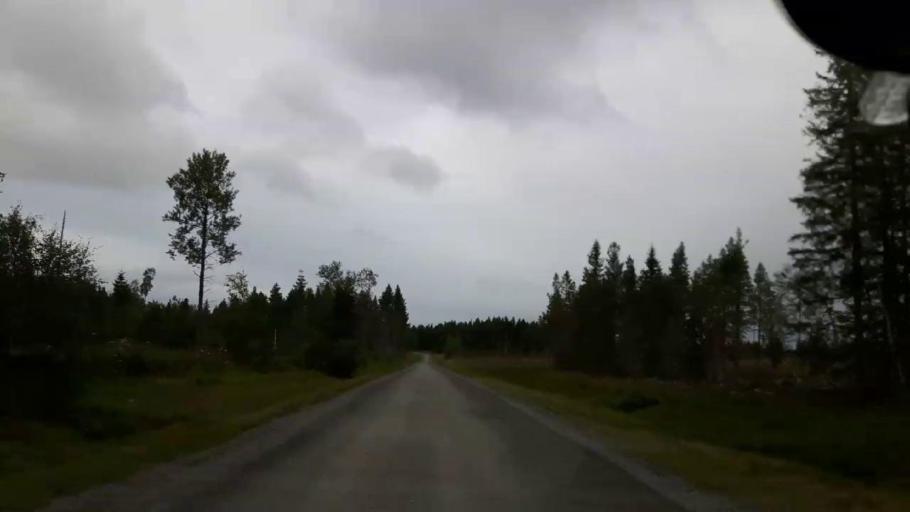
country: SE
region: Jaemtland
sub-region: OEstersunds Kommun
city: Ostersund
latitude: 63.1130
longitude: 14.5447
